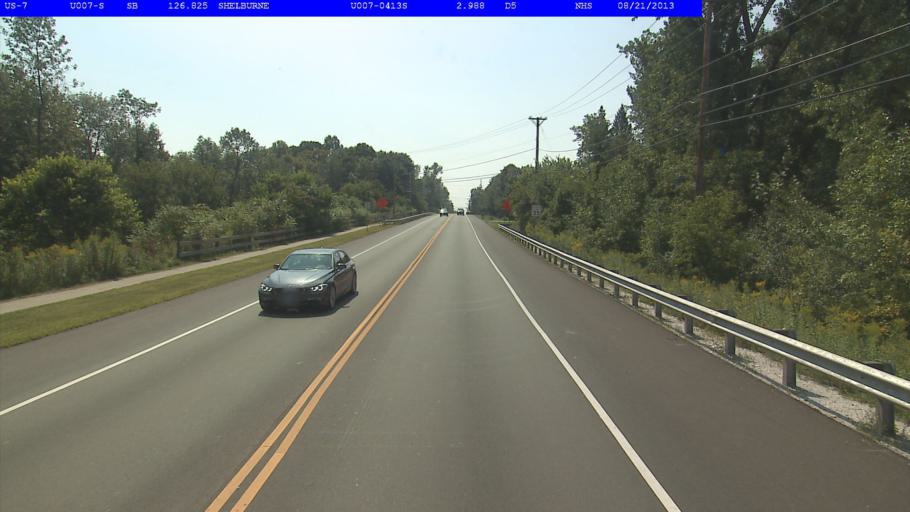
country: US
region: Vermont
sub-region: Chittenden County
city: Burlington
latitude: 44.3858
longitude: -73.2257
